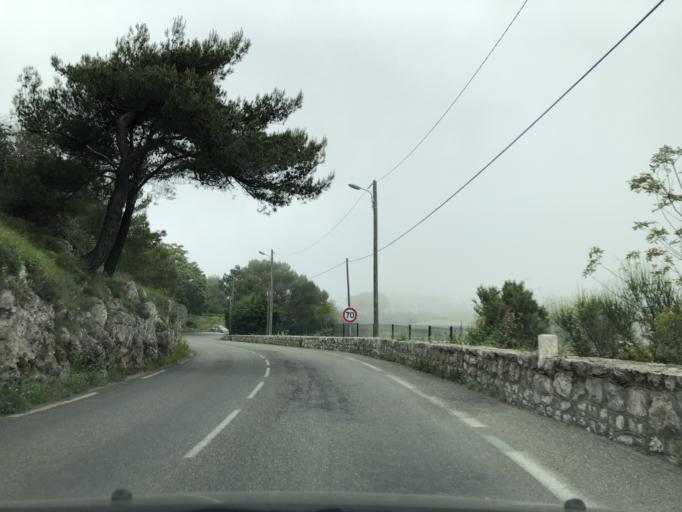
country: FR
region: Provence-Alpes-Cote d'Azur
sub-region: Departement des Alpes-Maritimes
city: Beaulieu-sur-Mer
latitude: 43.7301
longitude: 7.3426
